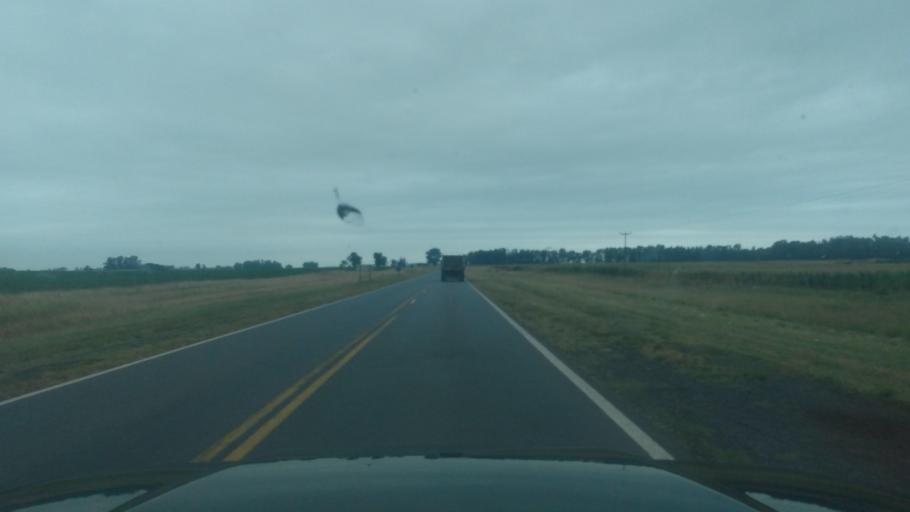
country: AR
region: Buenos Aires
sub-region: Partido de Nueve de Julio
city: Nueve de Julio
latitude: -35.4109
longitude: -60.7768
